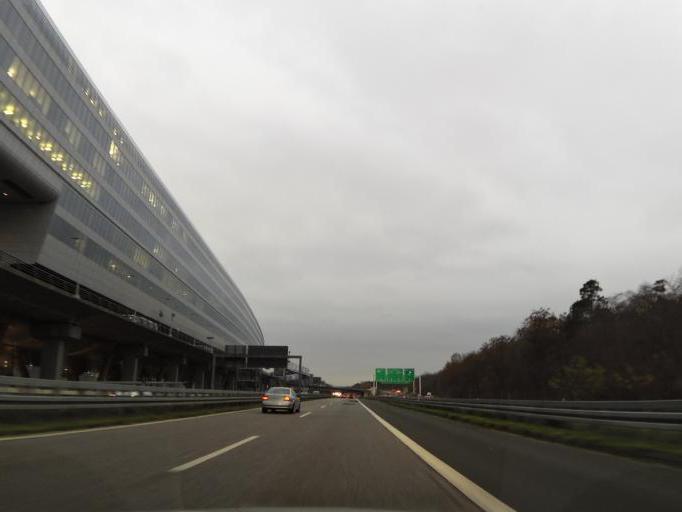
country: DE
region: Hesse
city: Kelsterbach
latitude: 50.0529
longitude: 8.5687
